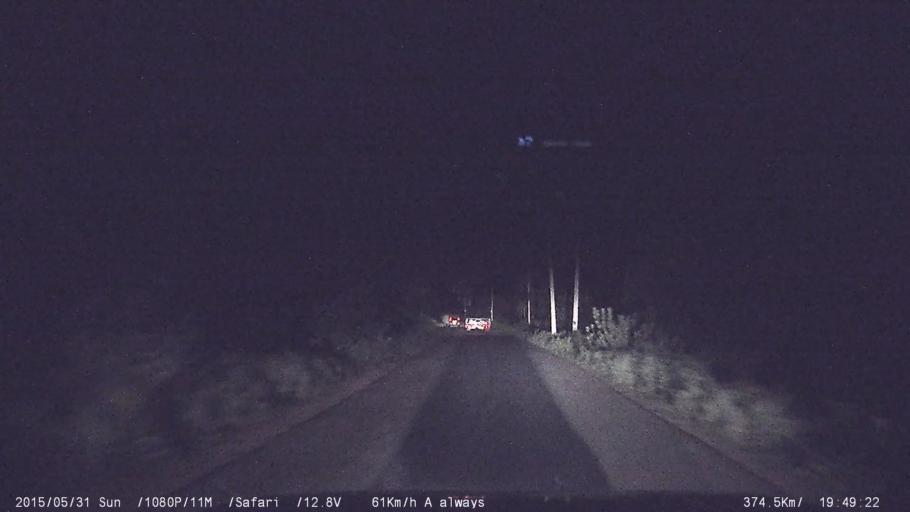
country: IN
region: Karnataka
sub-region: Mandya
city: Malavalli
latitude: 12.3170
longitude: 77.0720
